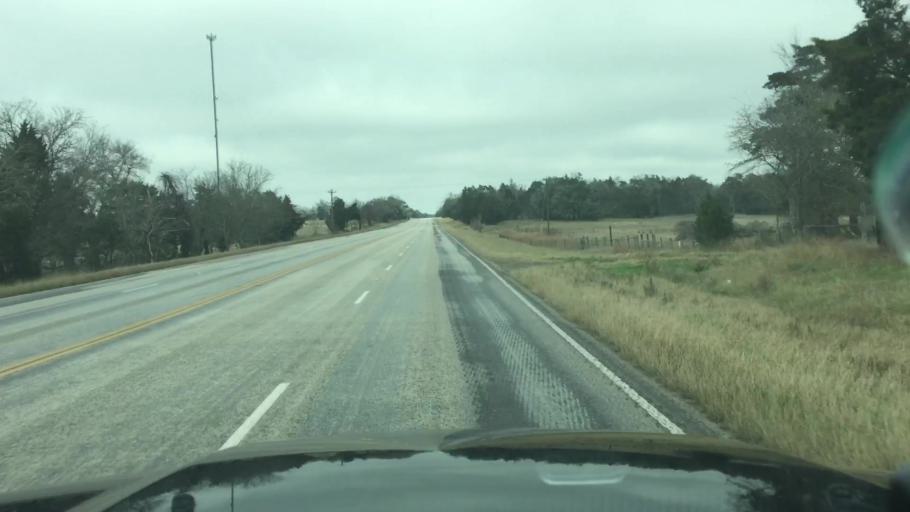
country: US
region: Texas
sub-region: Lee County
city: Giddings
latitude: 30.1054
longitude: -96.9143
